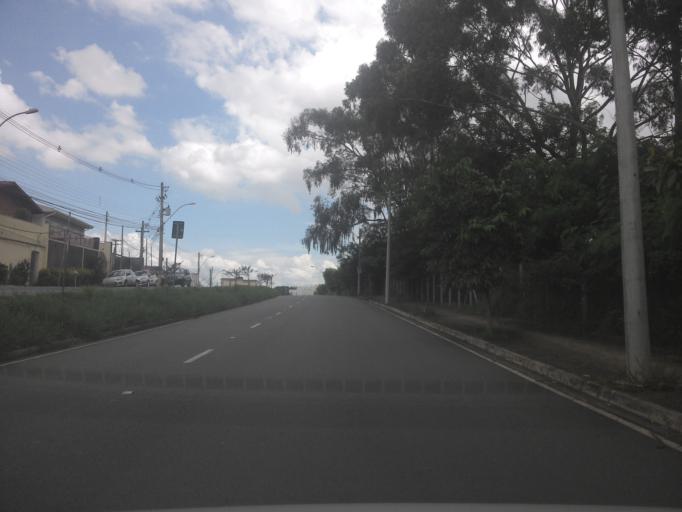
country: BR
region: Sao Paulo
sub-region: Campinas
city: Campinas
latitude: -22.8709
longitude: -47.0324
